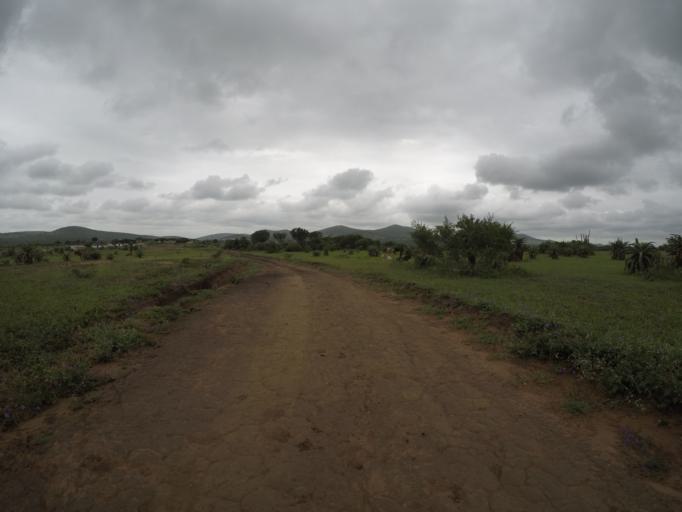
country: ZA
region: KwaZulu-Natal
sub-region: uThungulu District Municipality
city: Empangeni
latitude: -28.6048
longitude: 31.8644
